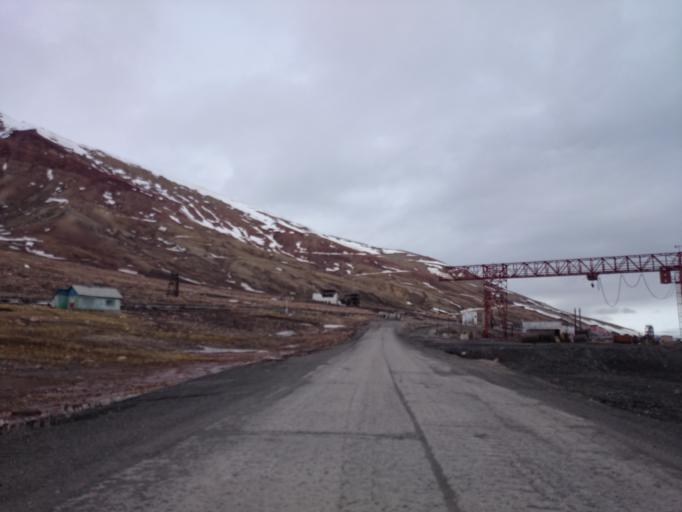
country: SJ
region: Svalbard
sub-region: Spitsbergen
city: Longyearbyen
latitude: 78.6546
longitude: 16.3501
